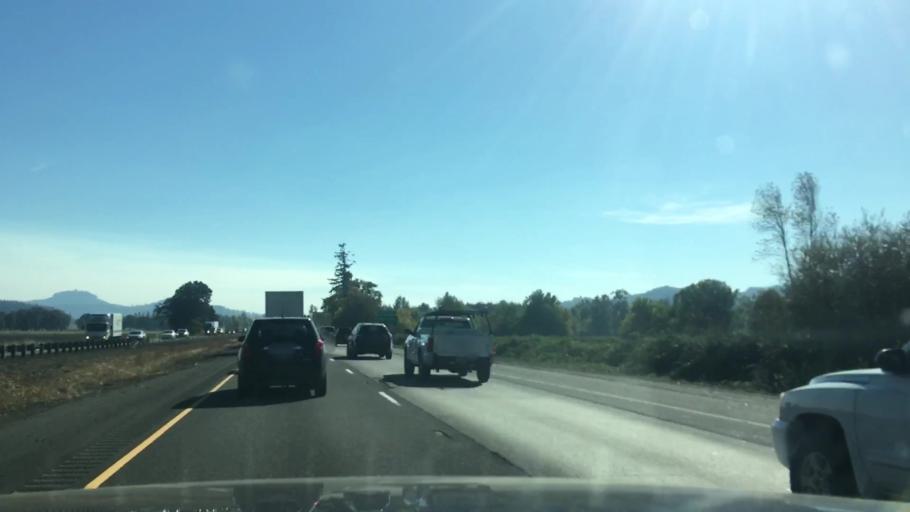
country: US
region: Oregon
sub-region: Lane County
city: Cottage Grove
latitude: 43.8470
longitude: -123.0231
